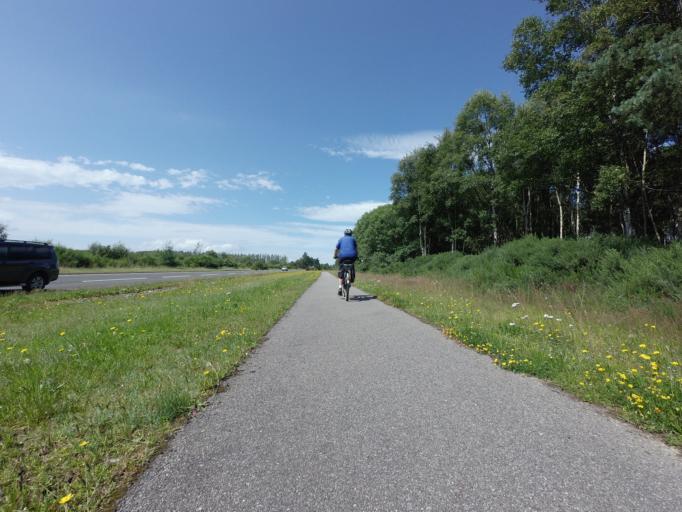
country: GB
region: Scotland
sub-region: Highland
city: Conon Bridge
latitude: 57.5392
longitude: -4.3697
